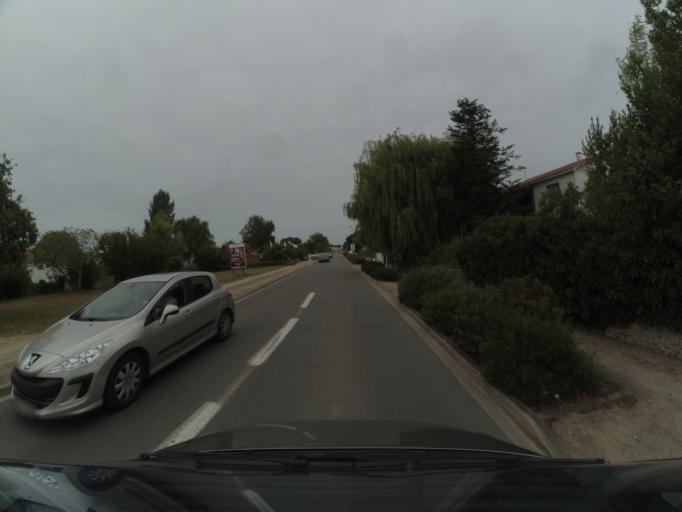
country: FR
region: Pays de la Loire
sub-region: Departement de la Vendee
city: La Barre-de-Monts
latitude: 46.8891
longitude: -2.1137
